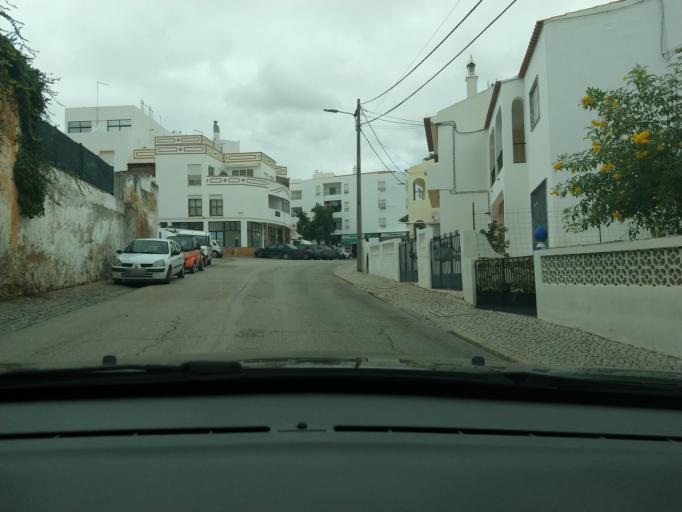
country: PT
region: Faro
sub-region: Lagoa
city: Lagoa
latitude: 37.1366
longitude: -8.4505
